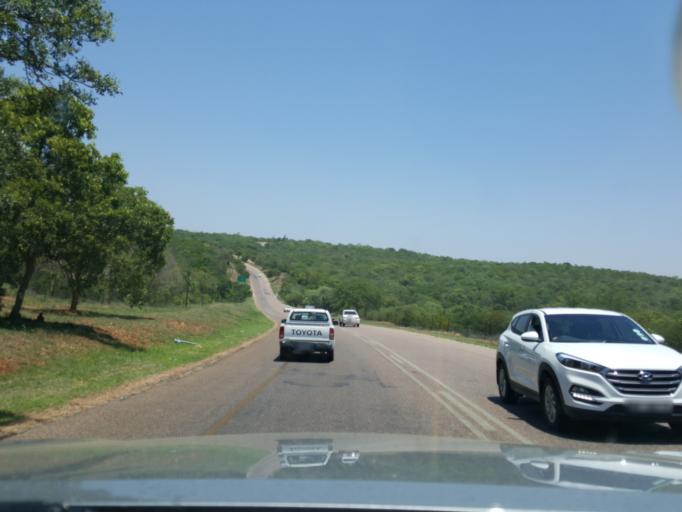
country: ZA
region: Limpopo
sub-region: Mopani District Municipality
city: Hoedspruit
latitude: -24.5446
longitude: 31.0377
